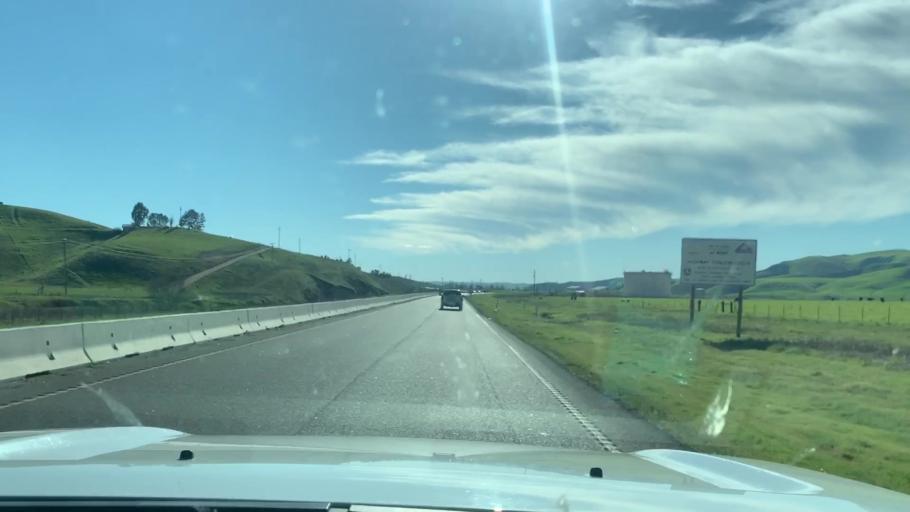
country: US
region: California
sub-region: San Luis Obispo County
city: Shandon
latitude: 35.6934
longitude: -120.3318
